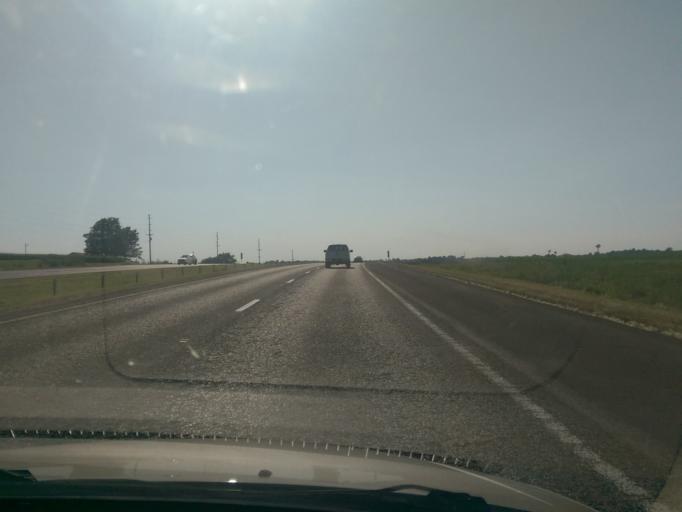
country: US
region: Missouri
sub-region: Lafayette County
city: Higginsville
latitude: 38.9930
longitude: -93.7067
